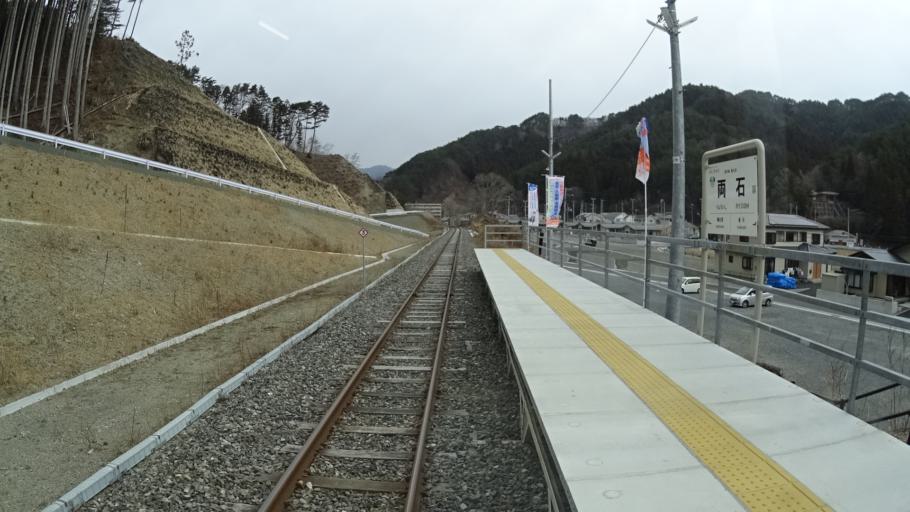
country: JP
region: Iwate
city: Kamaishi
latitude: 39.3083
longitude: 141.8889
